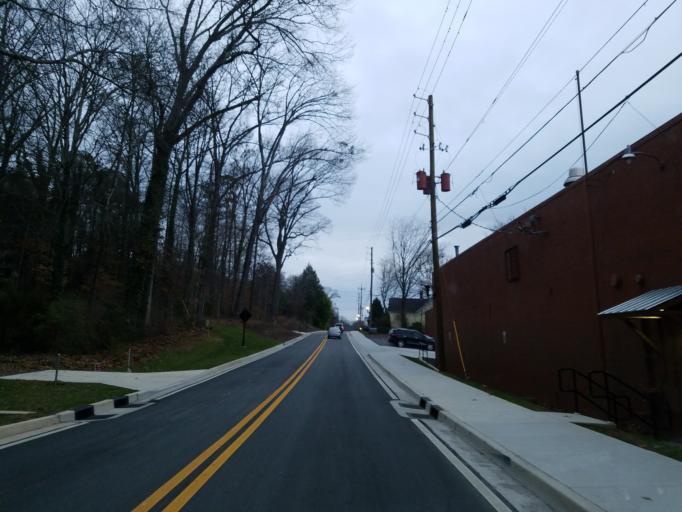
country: US
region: Georgia
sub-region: Cobb County
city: Acworth
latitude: 34.0651
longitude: -84.6734
